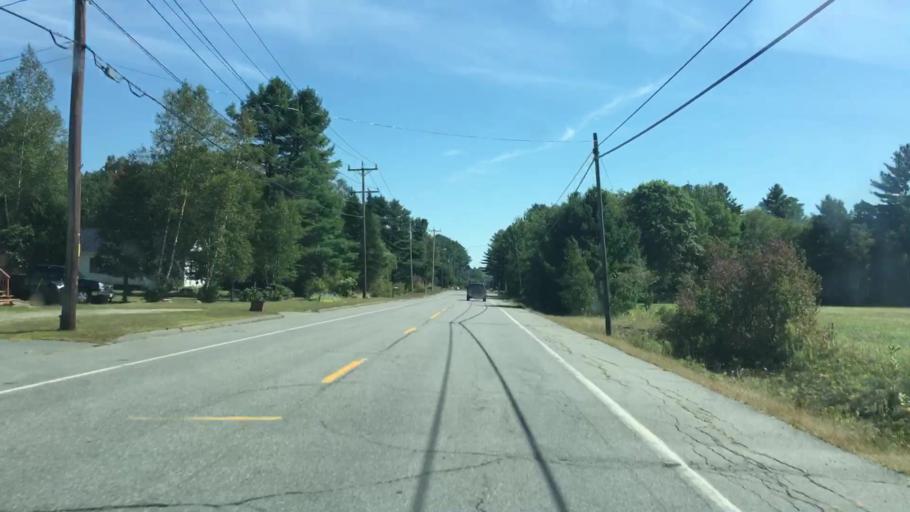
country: US
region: Maine
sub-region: Piscataquis County
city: Milo
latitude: 45.2417
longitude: -68.9713
